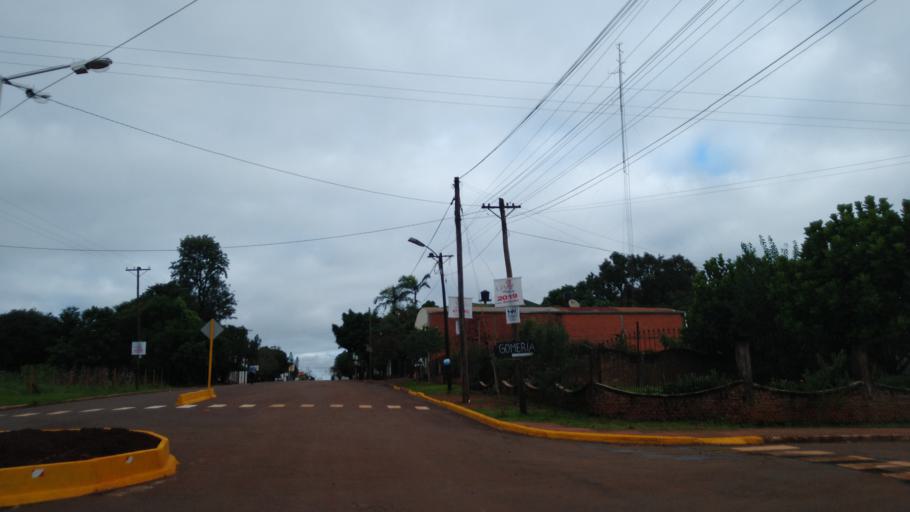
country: AR
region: Misiones
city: Jardin America
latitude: -27.0401
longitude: -55.2351
